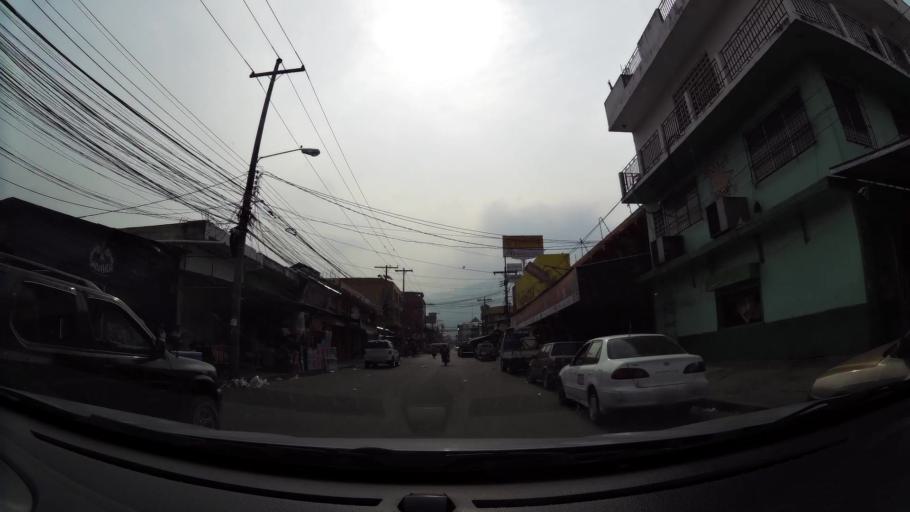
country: HN
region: Cortes
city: San Pedro Sula
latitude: 15.5000
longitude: -88.0218
